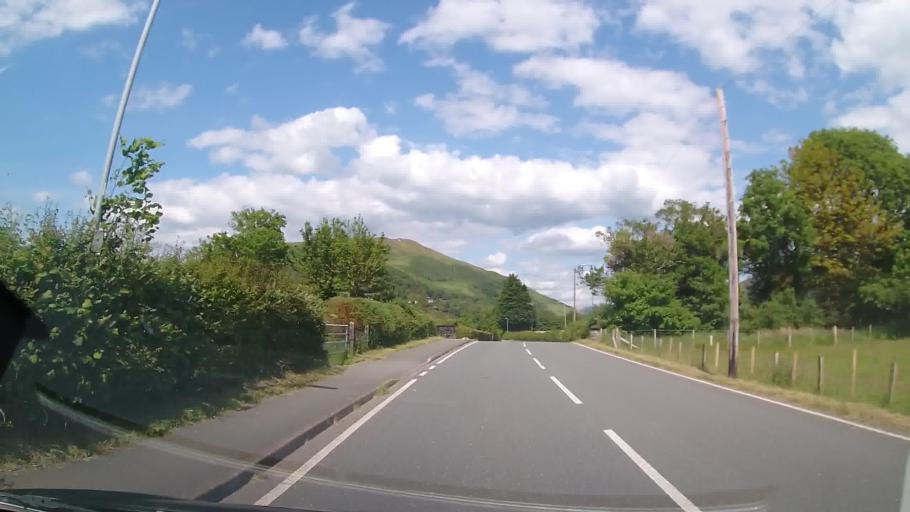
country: GB
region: Wales
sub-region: Gwynedd
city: Tywyn
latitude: 52.6064
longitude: -4.0512
